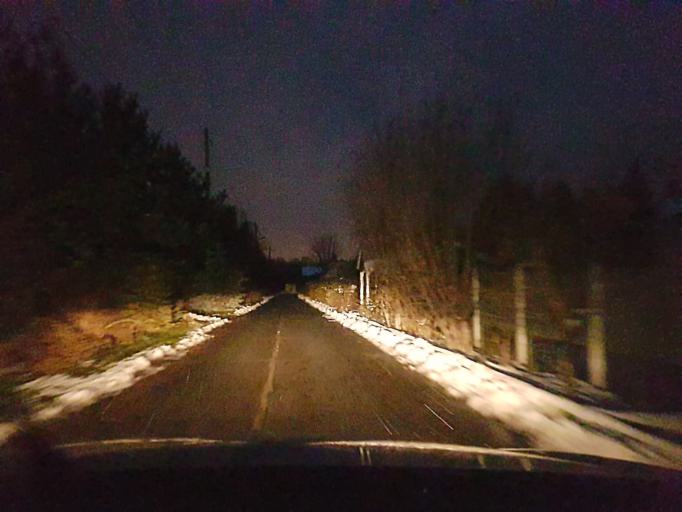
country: RU
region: Moskovskaya
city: Marfino
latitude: 56.0166
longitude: 37.5523
